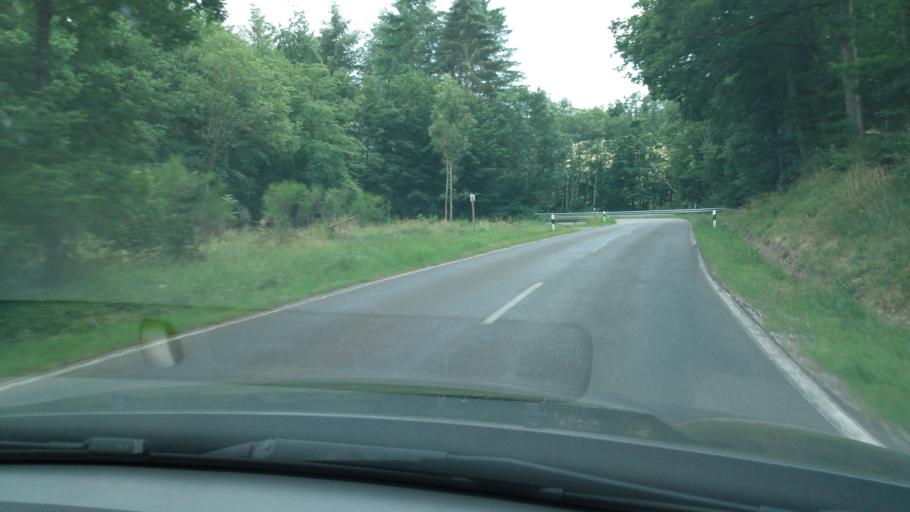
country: DE
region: Rheinland-Pfalz
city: Karl
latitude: 50.0605
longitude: 6.7944
